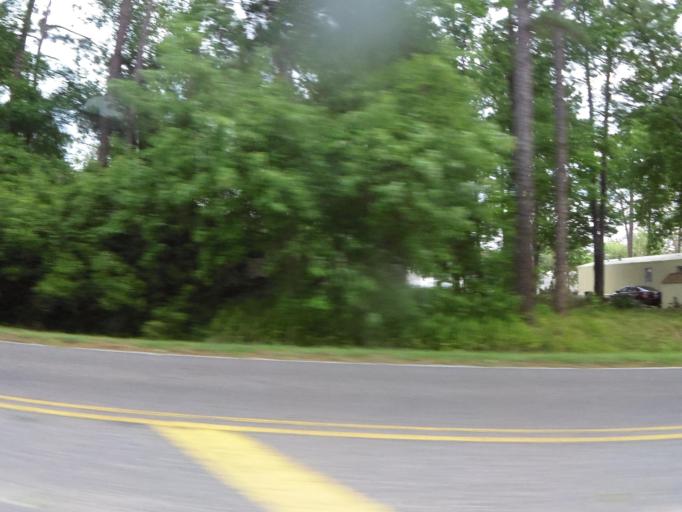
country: US
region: Florida
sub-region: Clay County
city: Bellair-Meadowbrook Terrace
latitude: 30.1937
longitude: -81.7179
